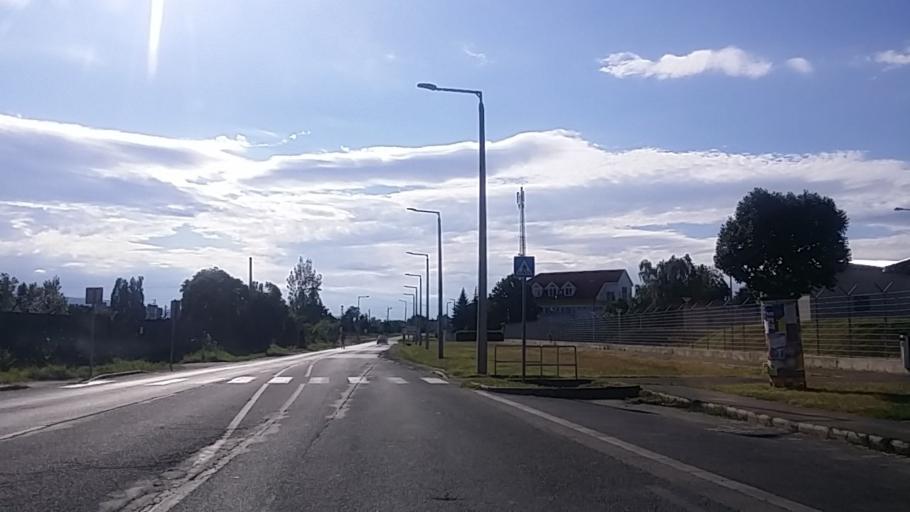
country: HU
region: Pest
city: Vac
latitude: 47.7732
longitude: 19.1530
